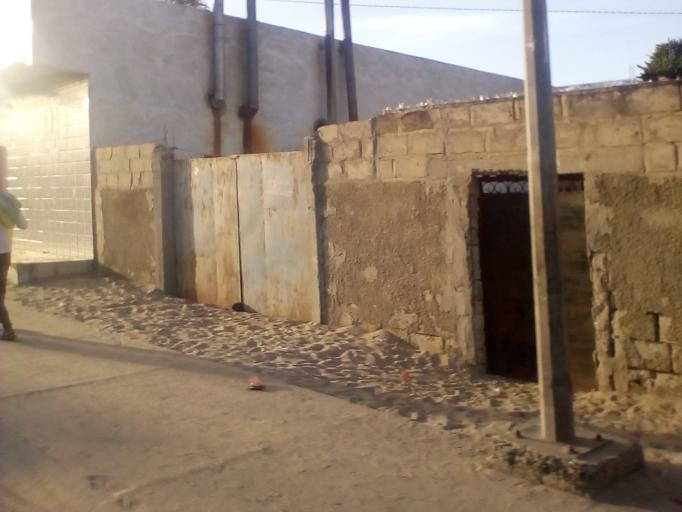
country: SN
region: Saint-Louis
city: Saint-Louis
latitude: 16.0191
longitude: -16.4857
